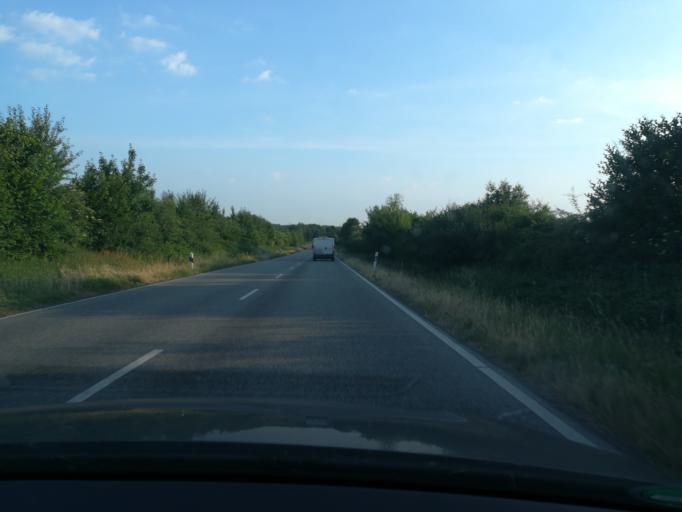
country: DE
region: Schleswig-Holstein
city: Siek
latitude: 53.6380
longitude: 10.3064
